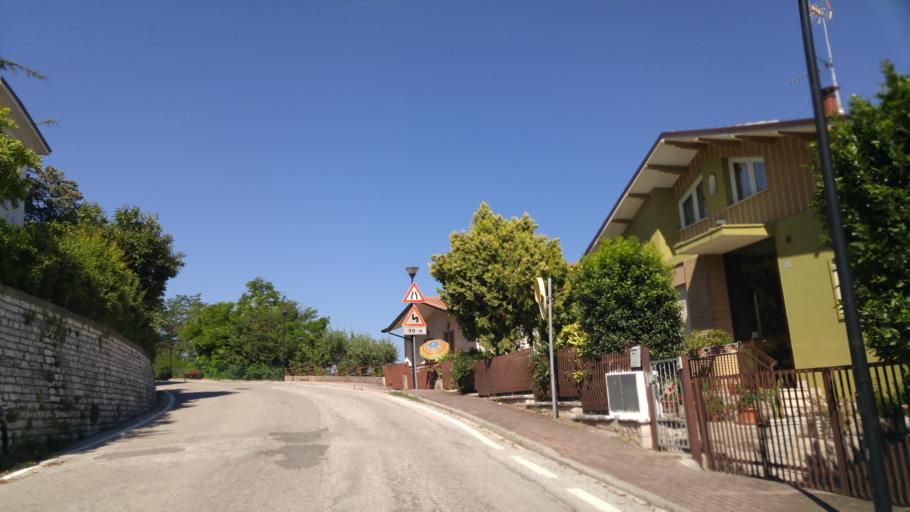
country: IT
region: The Marches
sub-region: Provincia di Pesaro e Urbino
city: Mombaroccio
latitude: 43.7946
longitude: 12.8551
